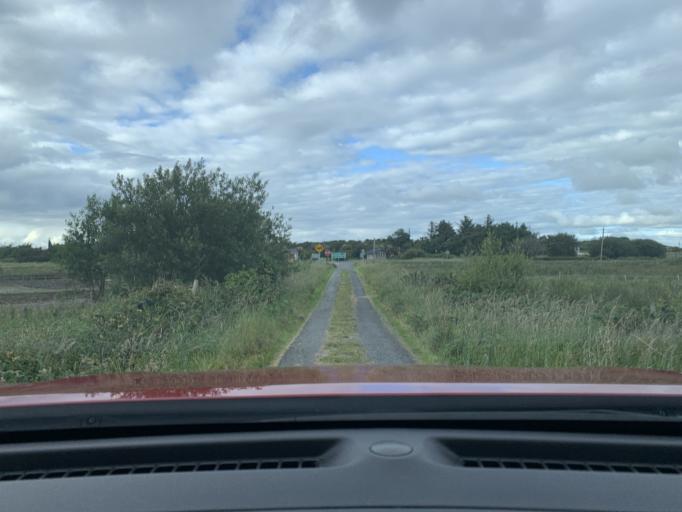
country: IE
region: Connaught
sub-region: County Leitrim
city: Kinlough
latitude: 54.4623
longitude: -8.3536
